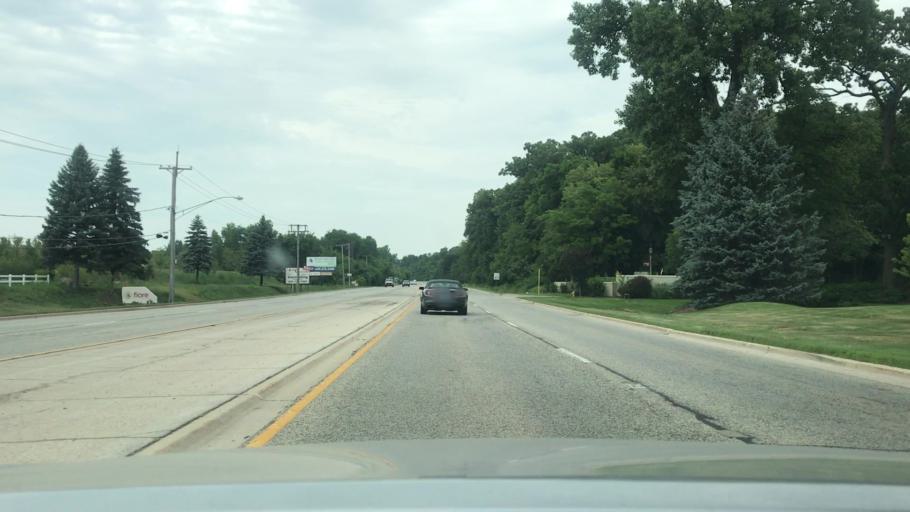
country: US
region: Illinois
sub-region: DuPage County
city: Woodridge
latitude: 41.7248
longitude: -88.0645
